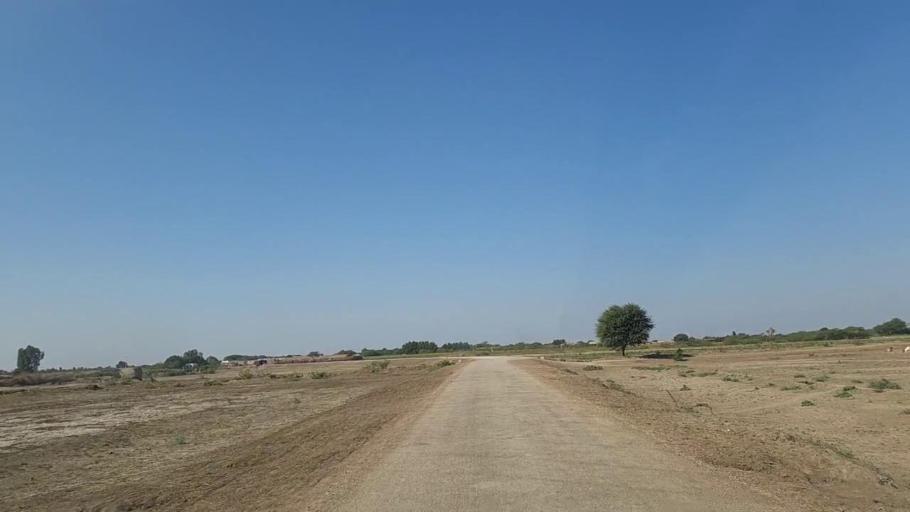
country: PK
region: Sindh
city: Naukot
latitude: 25.0079
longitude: 69.3406
